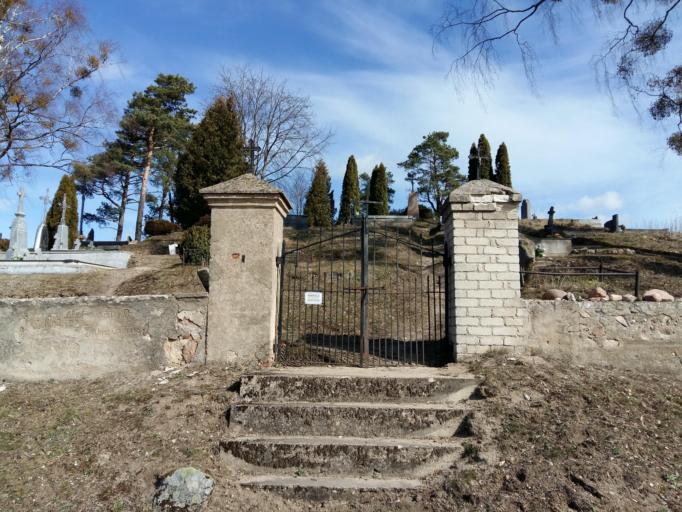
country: LT
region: Alytaus apskritis
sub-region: Alytaus rajonas
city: Daugai
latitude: 54.2500
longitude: 24.2779
